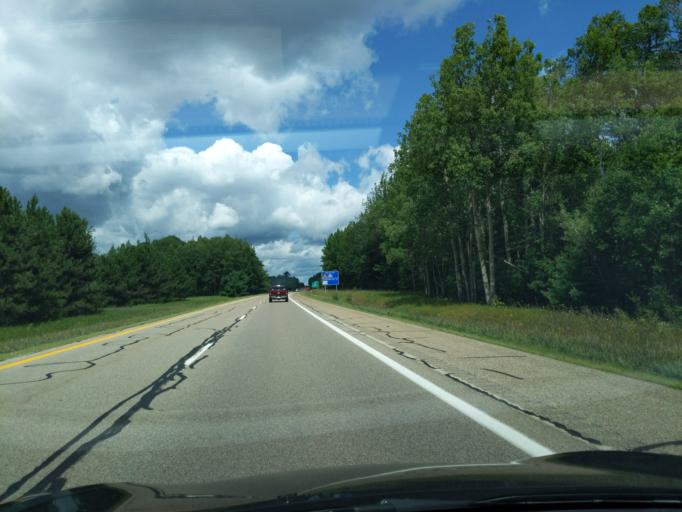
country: US
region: Michigan
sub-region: Roscommon County
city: Houghton Lake
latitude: 44.3116
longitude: -84.8053
